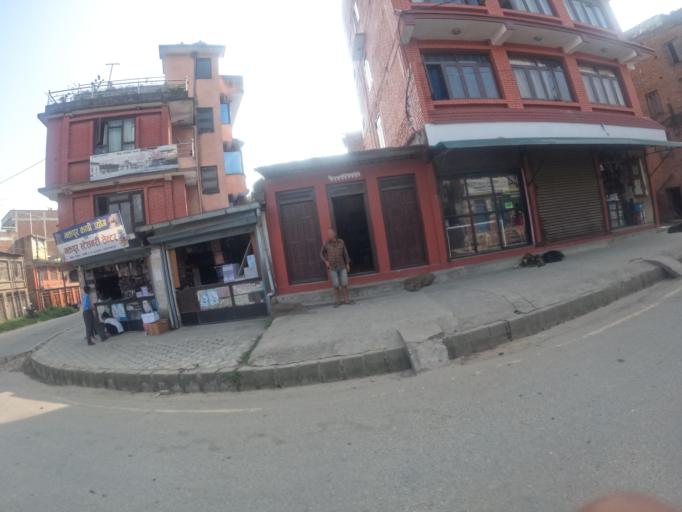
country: NP
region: Central Region
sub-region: Bagmati Zone
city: Bhaktapur
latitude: 27.6776
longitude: 85.4332
